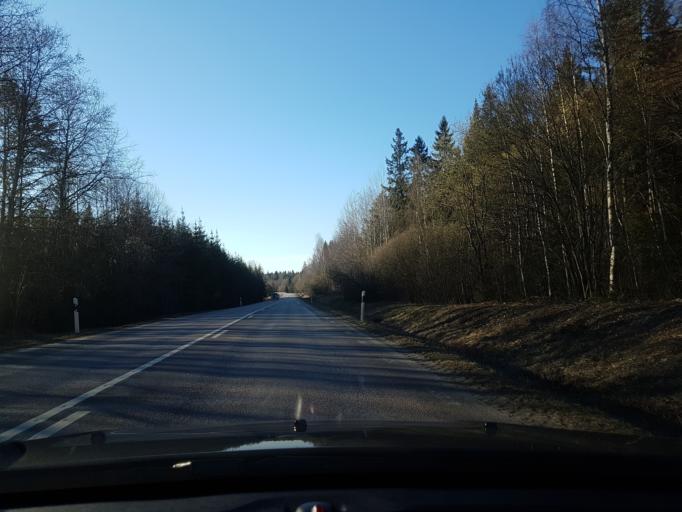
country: SE
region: Uppsala
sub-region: Heby Kommun
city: Morgongava
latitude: 59.9124
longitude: 17.0296
